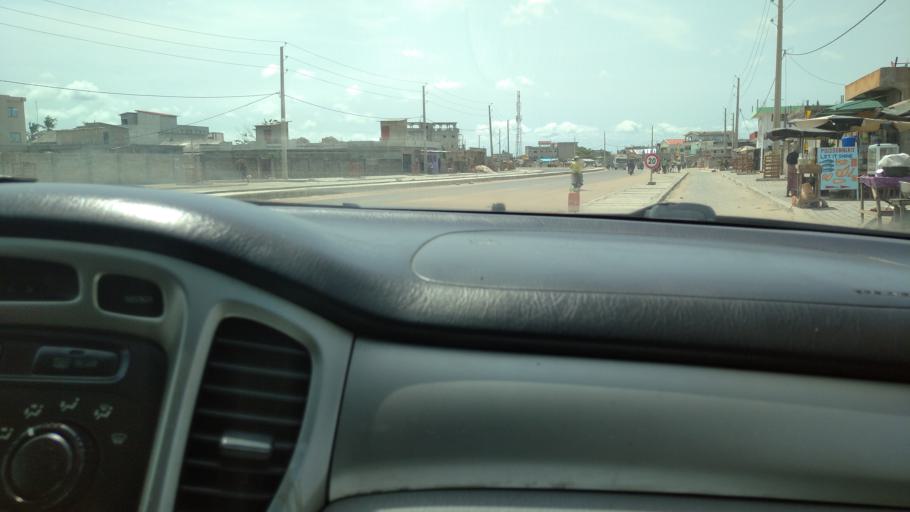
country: BJ
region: Littoral
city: Cotonou
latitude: 6.3712
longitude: 2.5000
